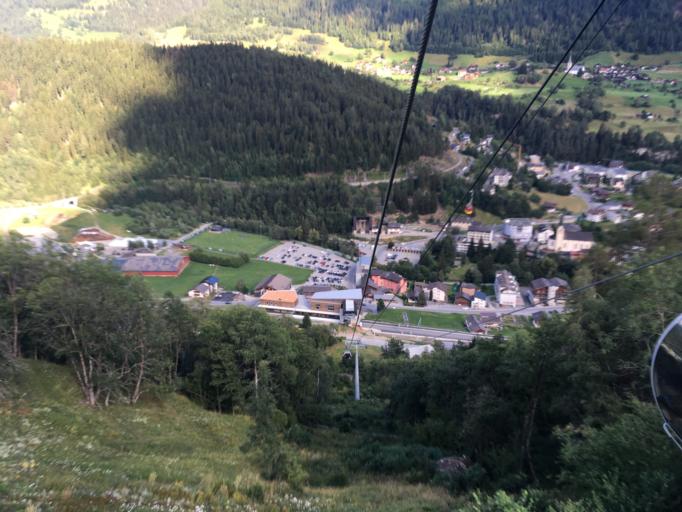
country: CH
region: Valais
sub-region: Goms District
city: Fiesch
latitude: 46.4072
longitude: 8.1293
